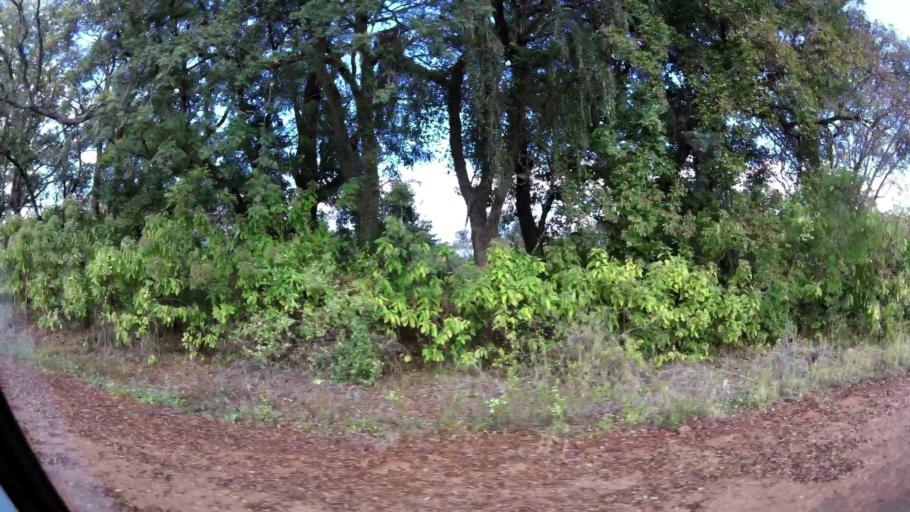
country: ZA
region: Limpopo
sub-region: Mopani District Municipality
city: Tzaneen
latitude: -23.7952
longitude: 30.1417
